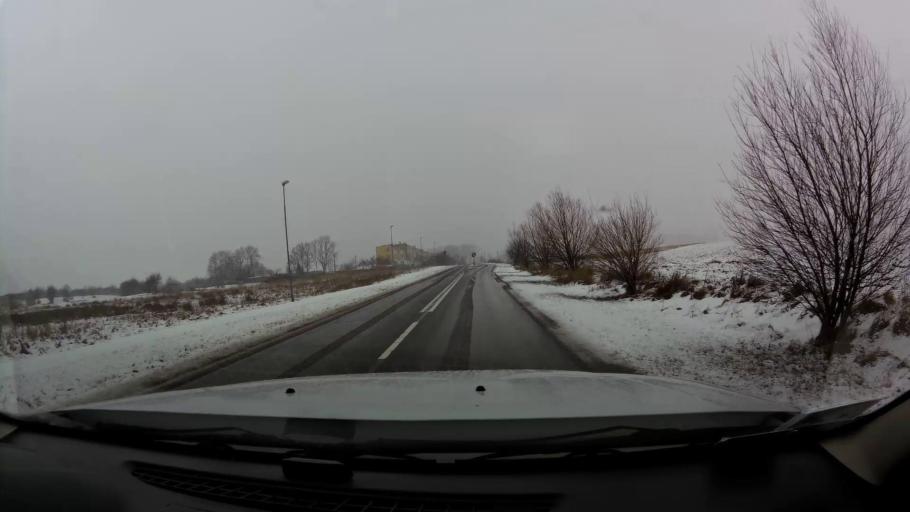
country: PL
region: West Pomeranian Voivodeship
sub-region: Powiat gryficki
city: Trzebiatow
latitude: 54.0952
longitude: 15.2664
